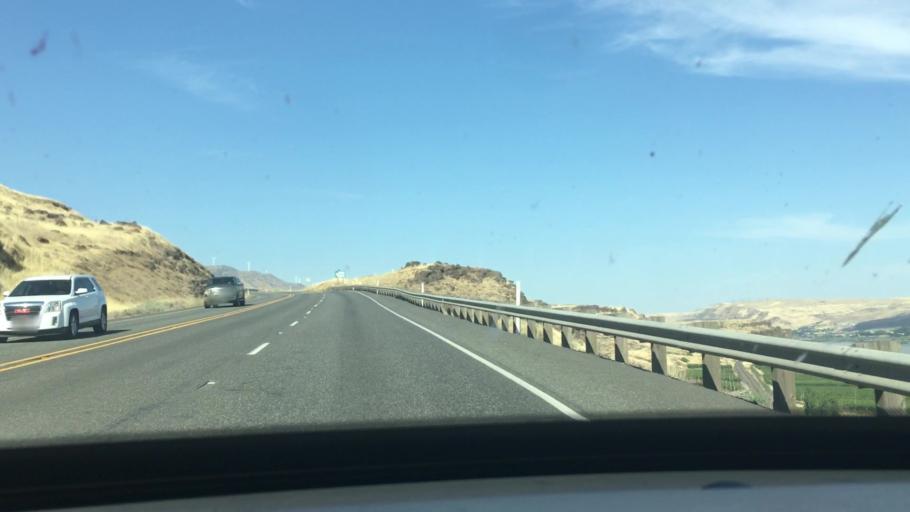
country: US
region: Washington
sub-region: Klickitat County
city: Goldendale
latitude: 45.6887
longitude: -120.8225
